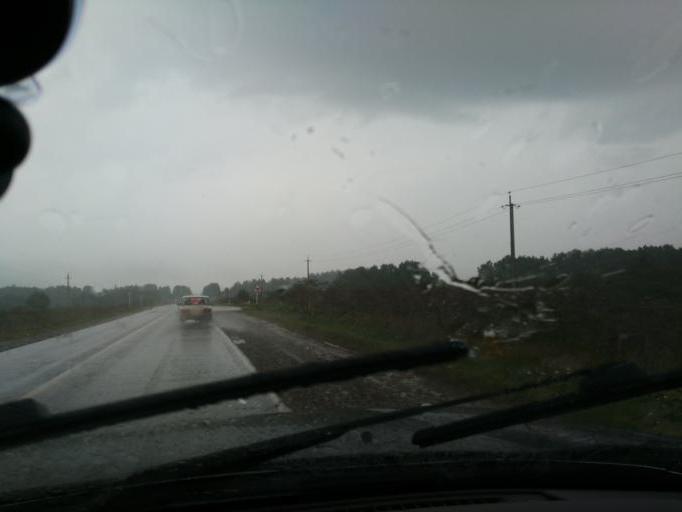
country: RU
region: Perm
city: Osa
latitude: 57.1541
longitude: 55.5296
